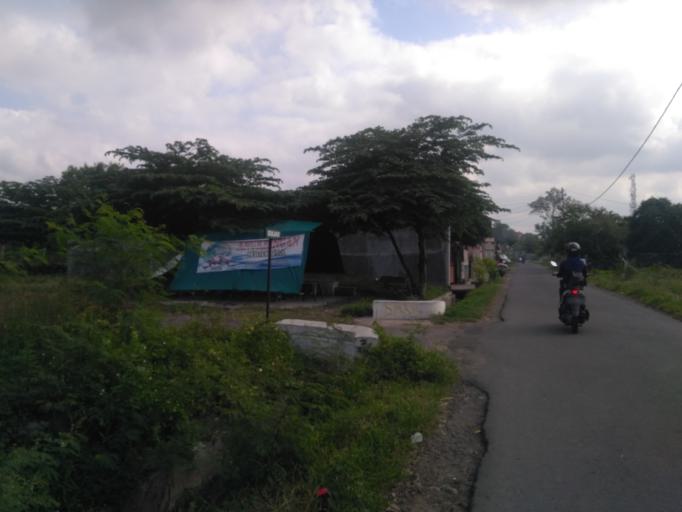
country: ID
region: Daerah Istimewa Yogyakarta
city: Yogyakarta
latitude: -7.7676
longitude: 110.3590
